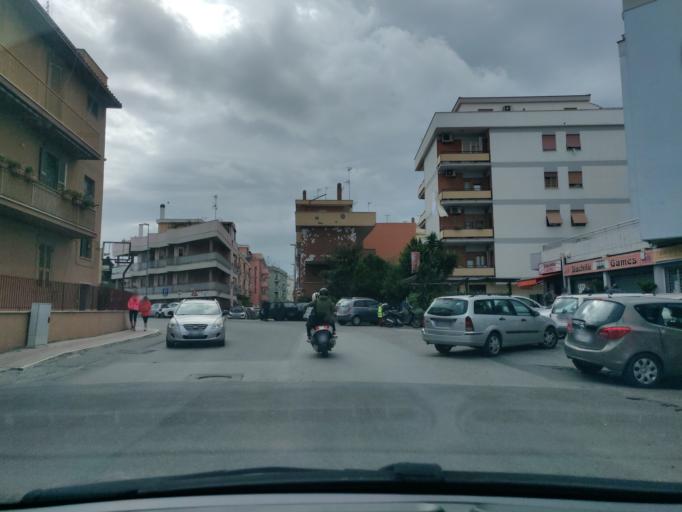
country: IT
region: Latium
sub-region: Citta metropolitana di Roma Capitale
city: Civitavecchia
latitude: 42.0950
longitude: 11.8037
